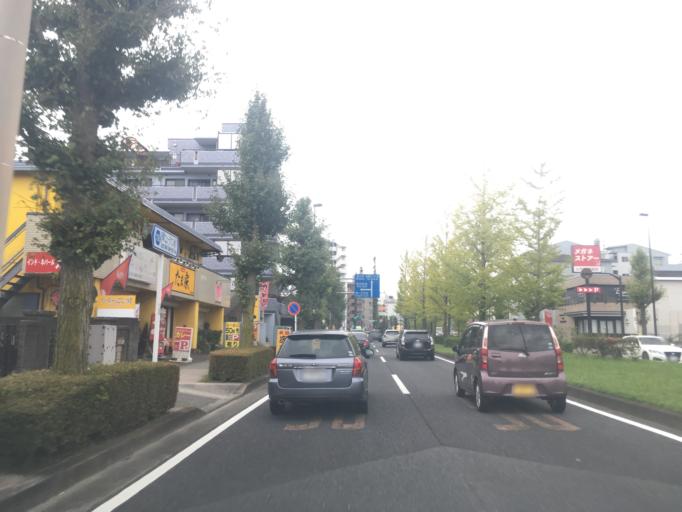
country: JP
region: Tokyo
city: Hino
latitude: 35.6291
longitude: 139.4303
